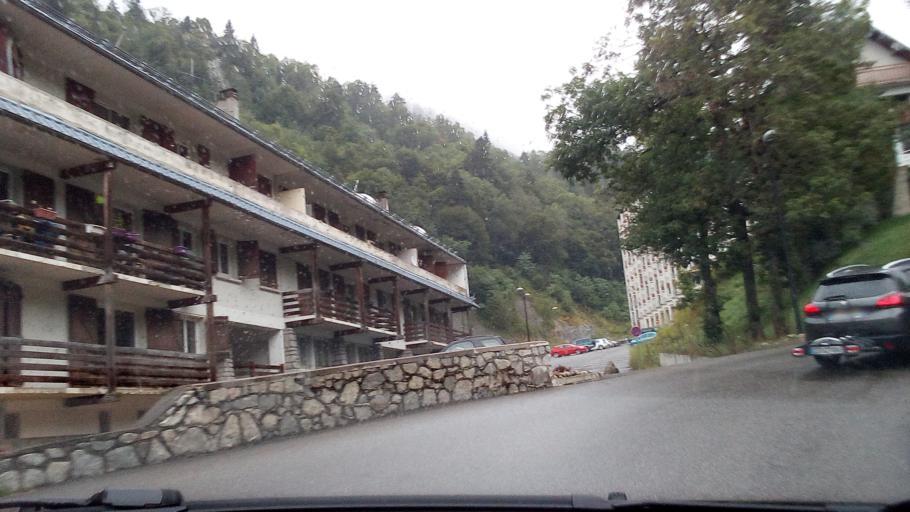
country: FR
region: Midi-Pyrenees
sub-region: Departement des Hautes-Pyrenees
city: Luz-Saint-Sauveur
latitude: 42.8956
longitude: 0.0587
